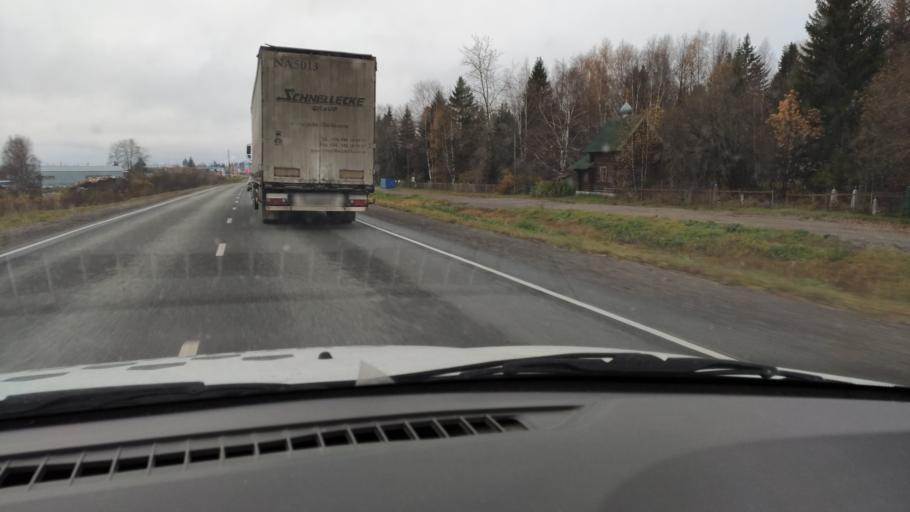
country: RU
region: Kirov
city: Omutninsk
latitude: 58.6917
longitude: 52.1946
